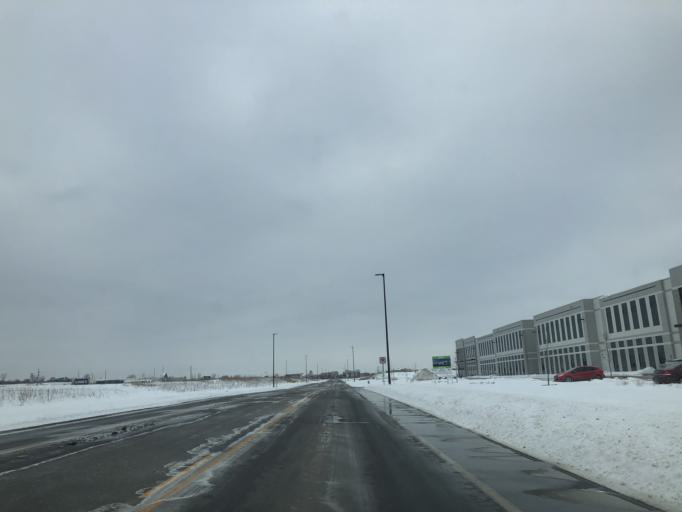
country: US
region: Minnesota
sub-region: Hennepin County
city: Osseo
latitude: 45.0920
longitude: -93.4139
